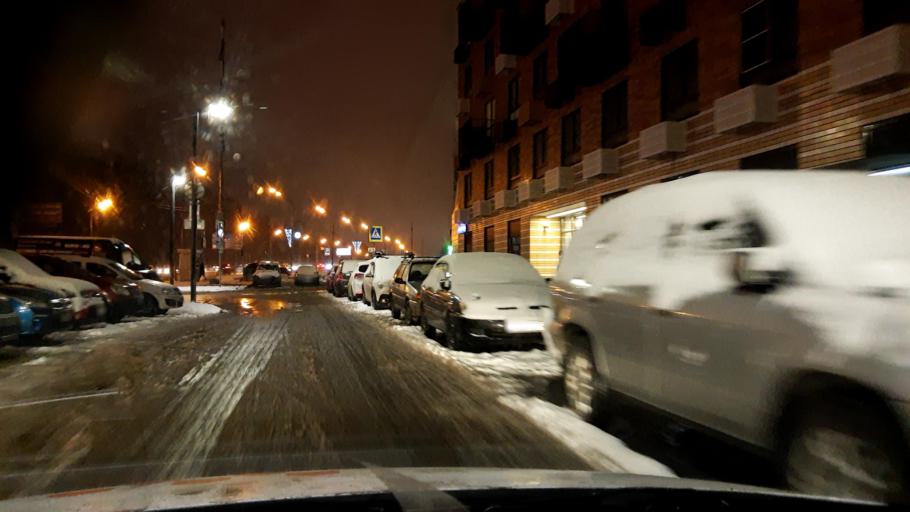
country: RU
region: Moscow
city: Annino
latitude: 55.5552
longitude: 37.5538
